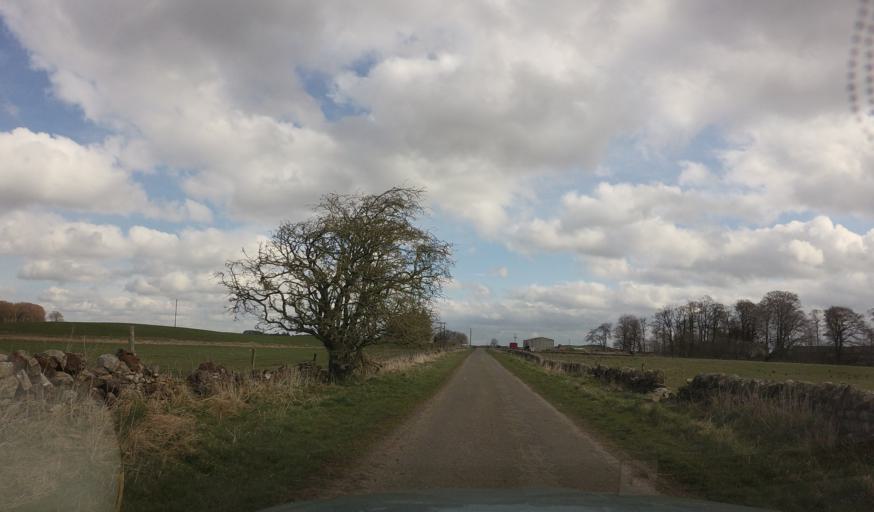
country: GB
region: Scotland
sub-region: Midlothian
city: Penicuik
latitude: 55.7988
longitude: -3.1663
